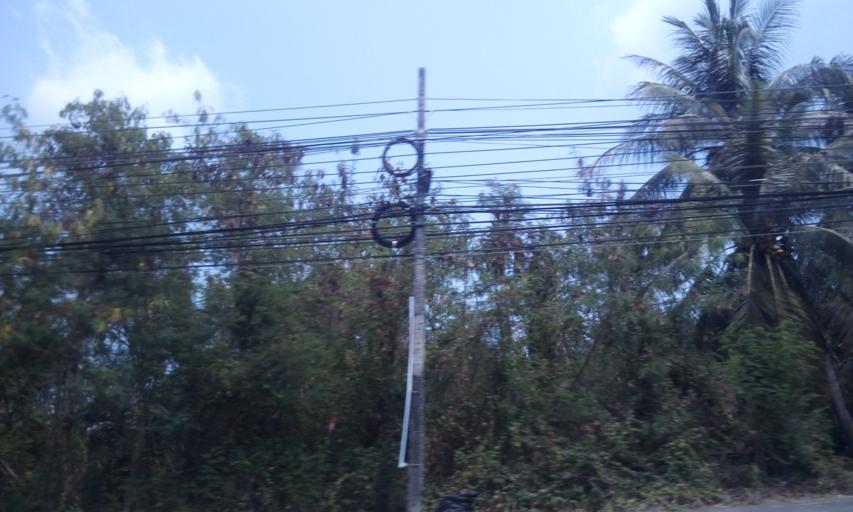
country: TH
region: Chachoengsao
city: Chachoengsao
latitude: 13.6789
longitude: 101.0825
